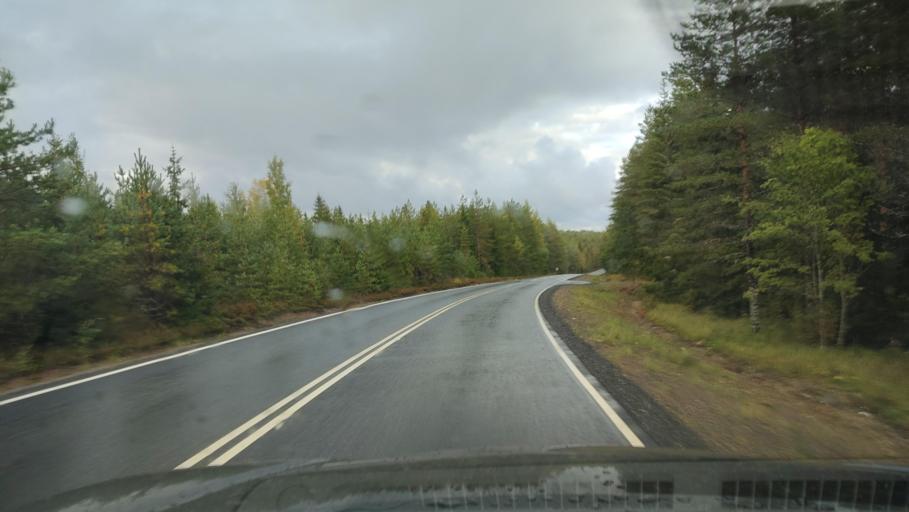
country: FI
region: Southern Ostrobothnia
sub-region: Suupohja
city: Karijoki
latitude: 62.2934
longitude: 21.6620
